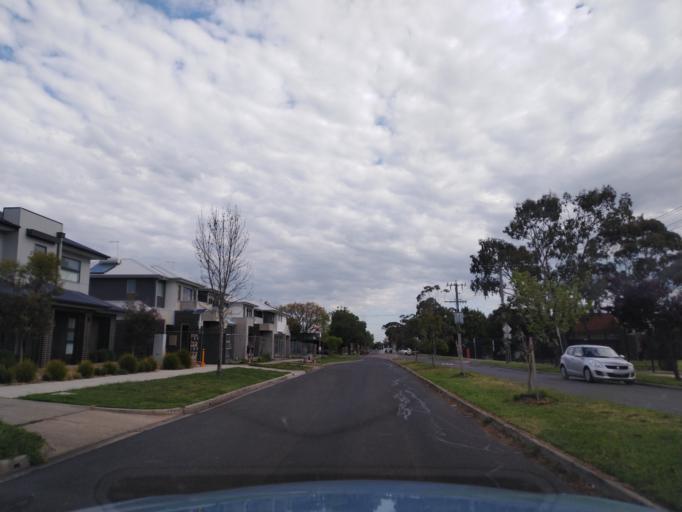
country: AU
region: Victoria
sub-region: Hobsons Bay
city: South Kingsville
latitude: -37.8435
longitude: 144.8640
